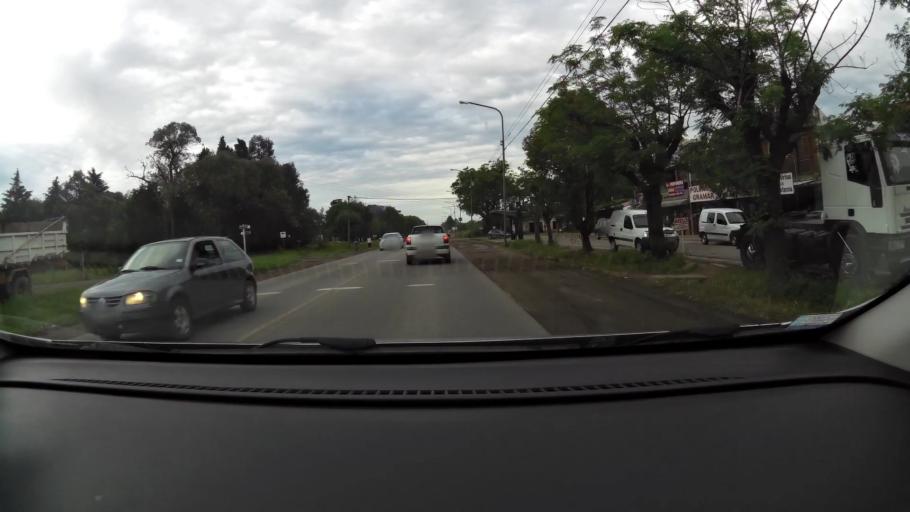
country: AR
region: Buenos Aires
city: San Nicolas de los Arroyos
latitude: -33.3745
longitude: -60.2050
